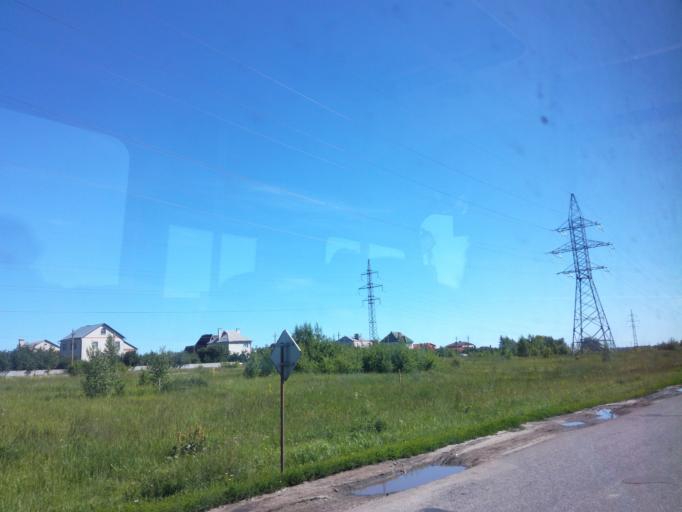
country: RU
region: Kursk
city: Kursk
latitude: 51.7909
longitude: 36.1704
